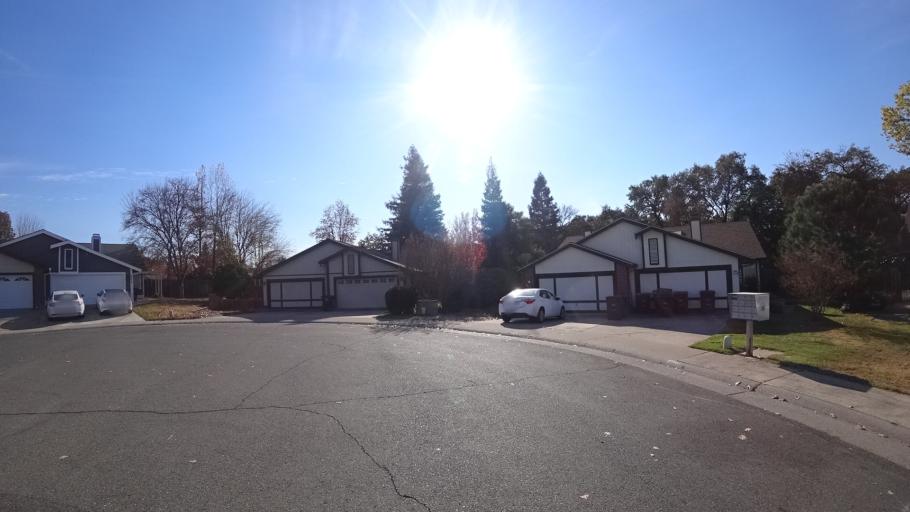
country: US
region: California
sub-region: Sacramento County
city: Citrus Heights
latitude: 38.6742
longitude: -121.2982
